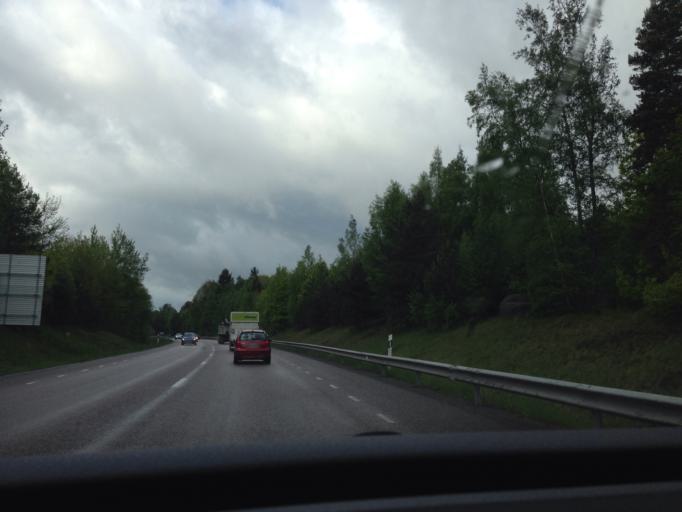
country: SE
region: Vaestra Goetaland
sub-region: Skovde Kommun
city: Skoevde
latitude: 58.4053
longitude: 13.8741
